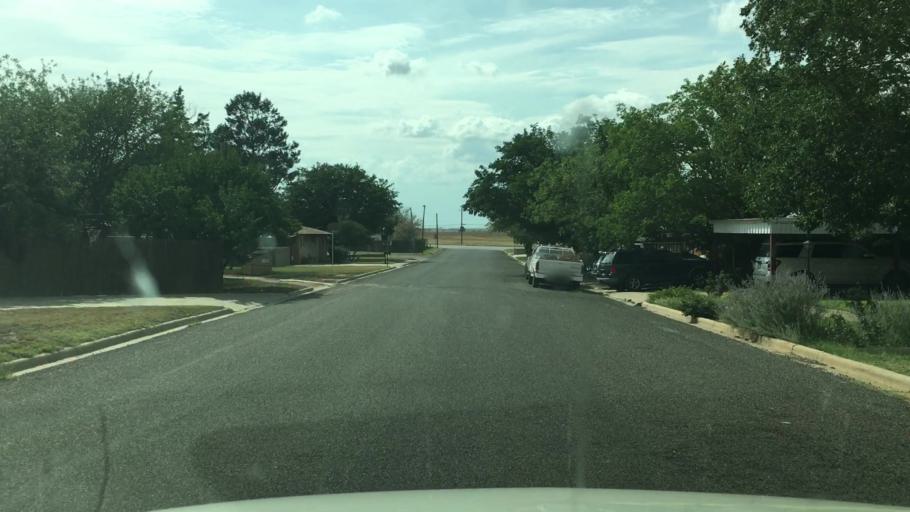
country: US
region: Texas
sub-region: Dawson County
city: Lamesa
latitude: 32.7528
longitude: -101.9551
